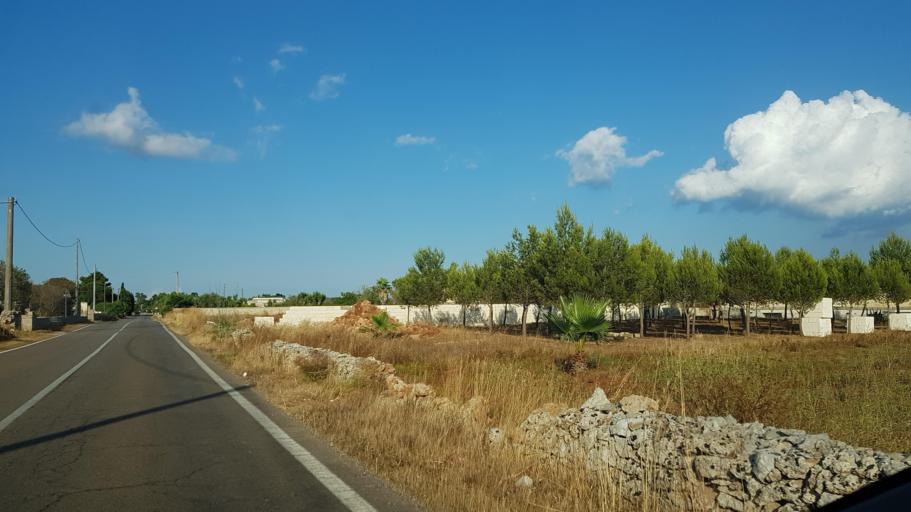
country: IT
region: Apulia
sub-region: Provincia di Lecce
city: Montesano Salentino
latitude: 39.9751
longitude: 18.3299
